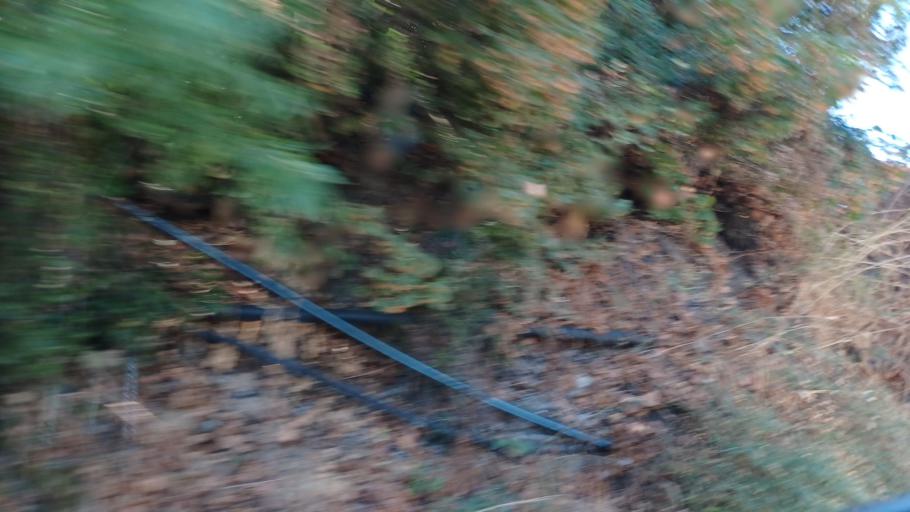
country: CY
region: Pafos
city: Mesogi
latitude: 34.9216
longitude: 32.6339
